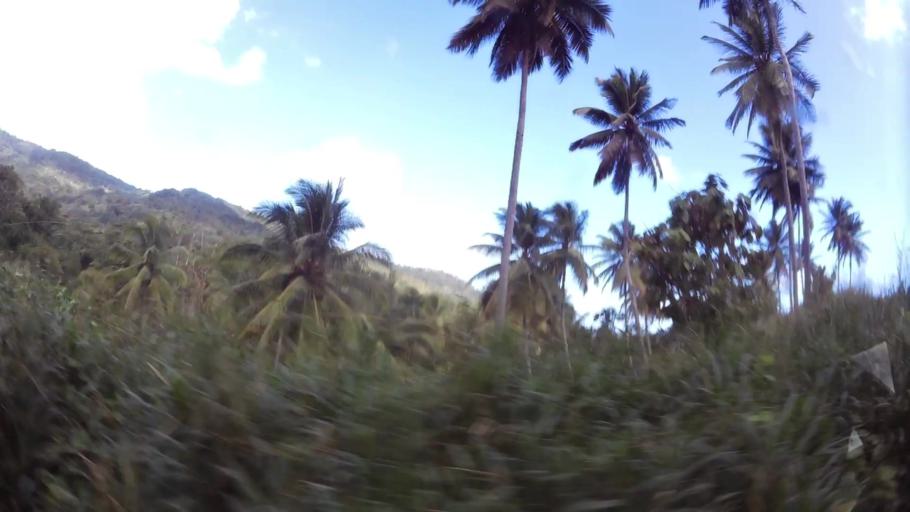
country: DM
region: Saint Andrew
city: Marigot
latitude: 15.5169
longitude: -61.2744
